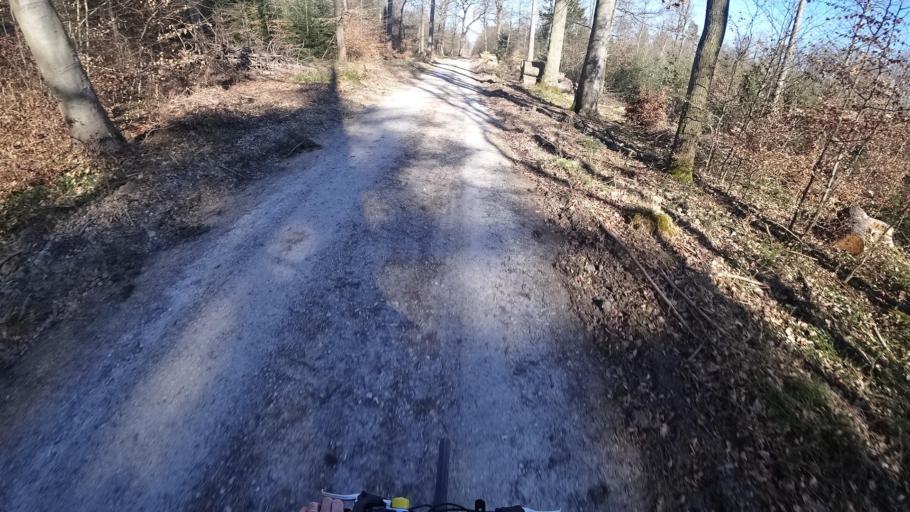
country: DE
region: Rheinland-Pfalz
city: Boppard
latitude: 50.2121
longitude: 7.5677
